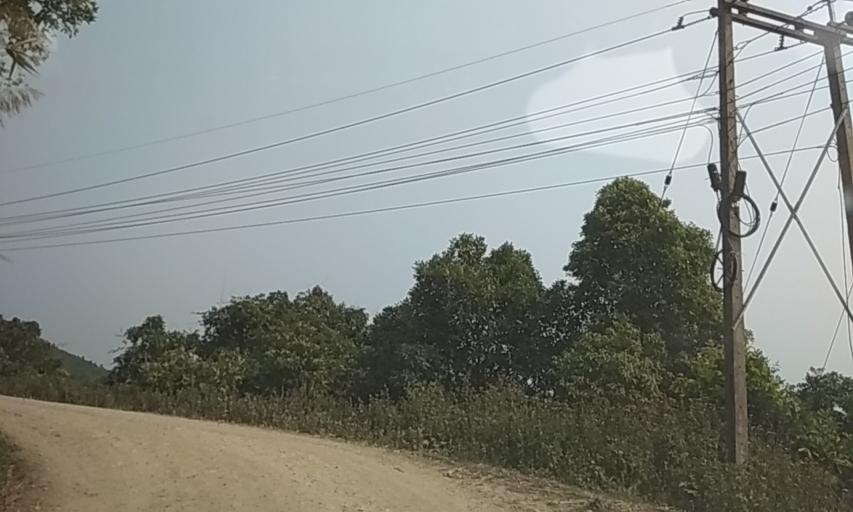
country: TH
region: Nan
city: Chaloem Phra Kiat
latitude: 20.0147
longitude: 101.1163
